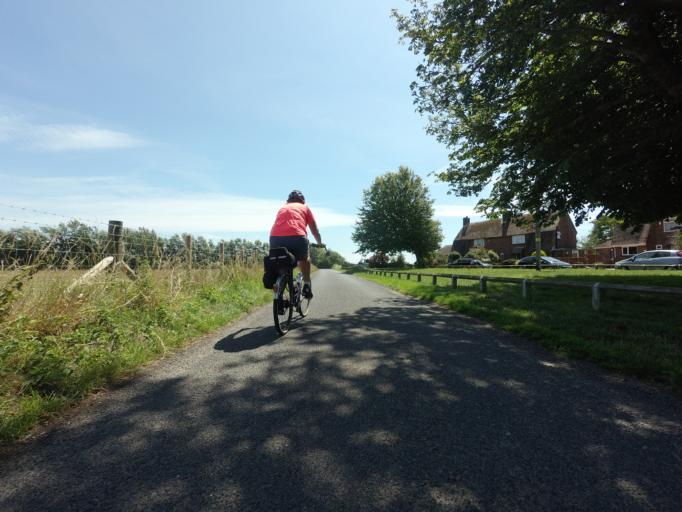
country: GB
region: England
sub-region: Kent
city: Lydd
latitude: 50.9884
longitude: 0.8936
